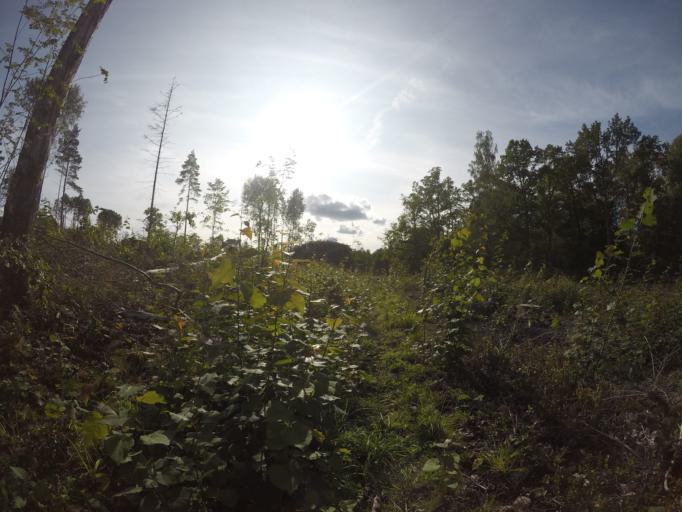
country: SE
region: Soedermanland
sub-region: Eskilstuna Kommun
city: Kvicksund
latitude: 59.5147
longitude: 16.3038
